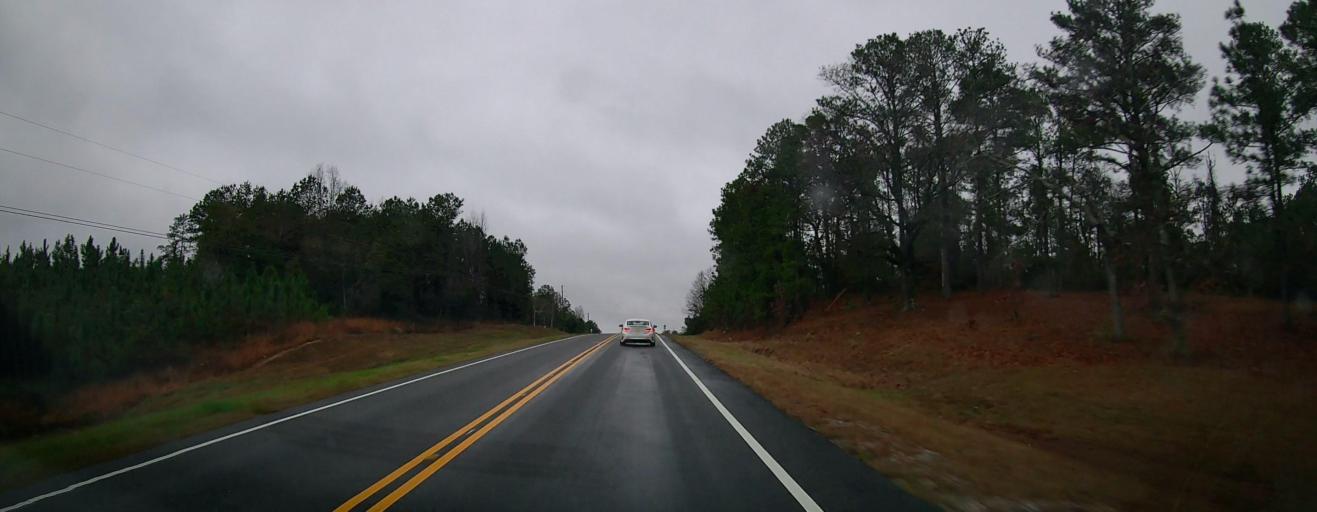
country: US
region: Alabama
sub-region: Chilton County
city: Clanton
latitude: 32.6887
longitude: -86.7939
